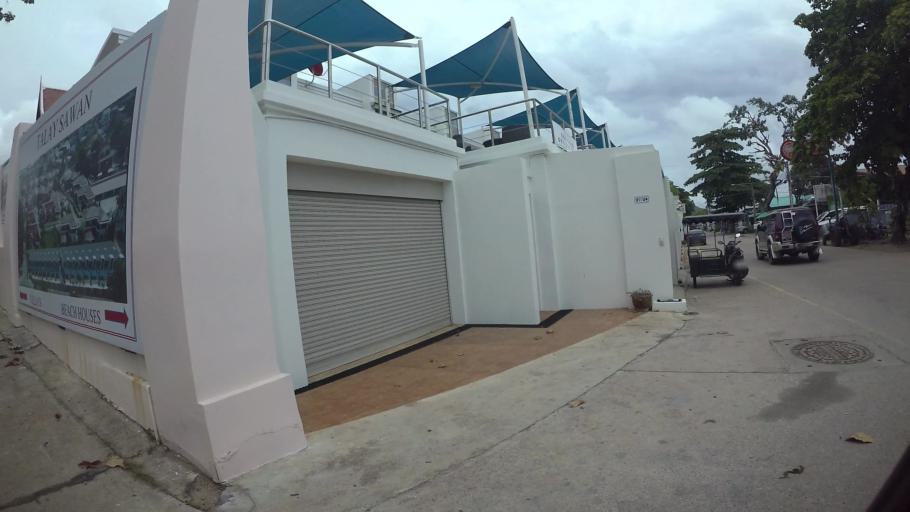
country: TH
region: Chon Buri
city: Sattahip
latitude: 12.7657
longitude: 100.8933
